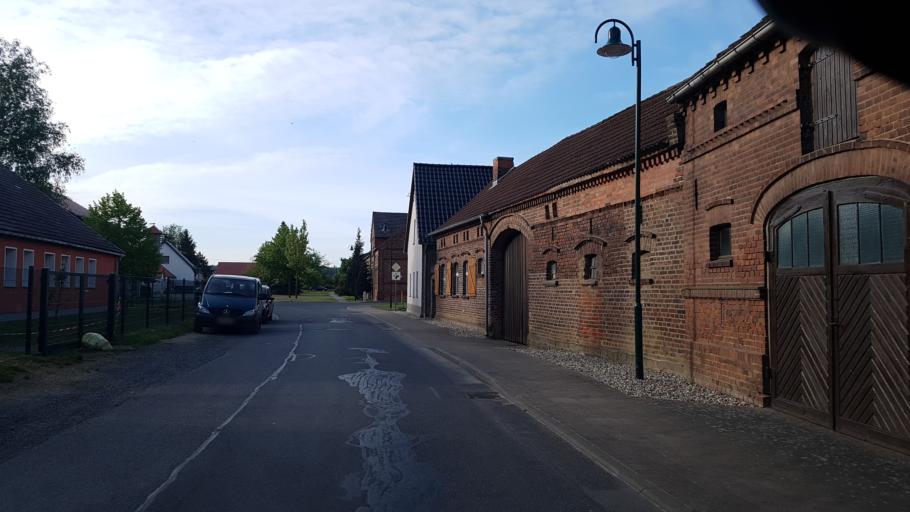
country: DE
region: Brandenburg
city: Dahme
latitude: 51.8636
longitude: 13.4614
